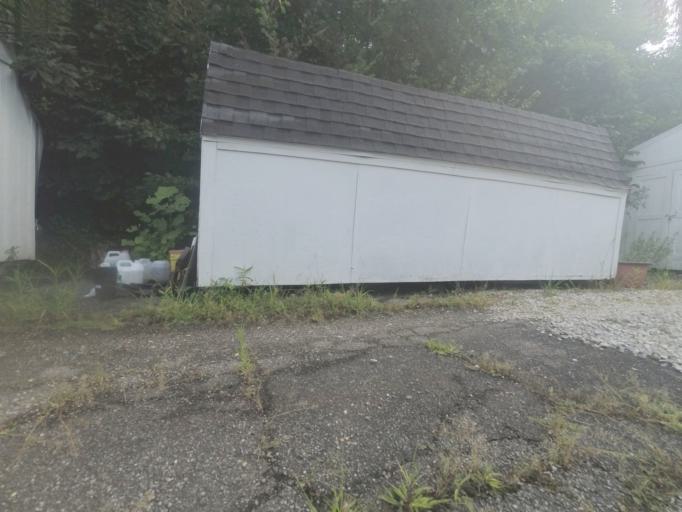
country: US
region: West Virginia
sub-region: Cabell County
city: Huntington
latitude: 38.3979
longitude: -82.4189
